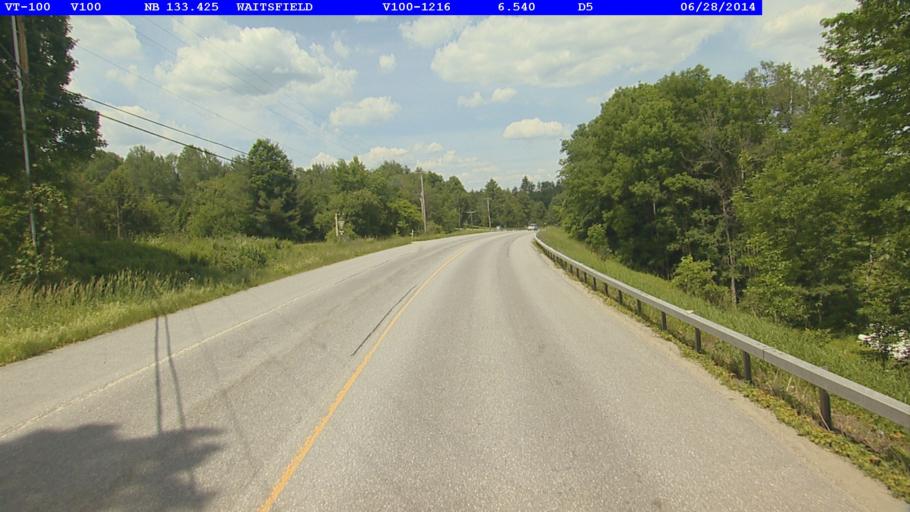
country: US
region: Vermont
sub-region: Washington County
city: Waterbury
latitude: 44.2220
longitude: -72.7898
